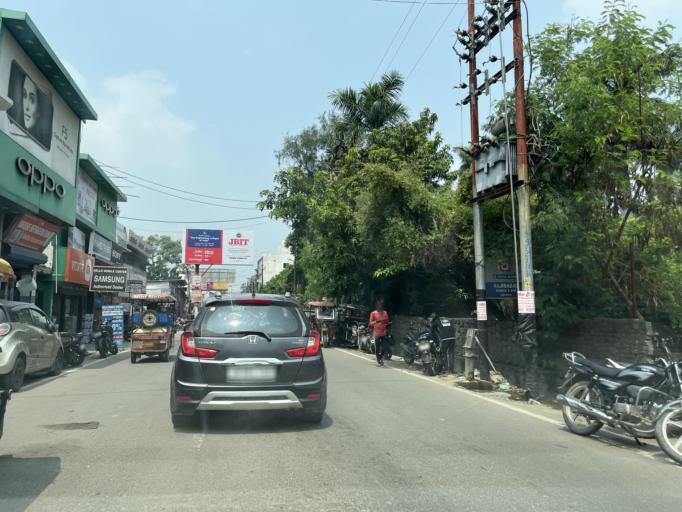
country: IN
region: Uttar Pradesh
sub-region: Bijnor
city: Najibabad
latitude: 29.6058
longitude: 78.3389
